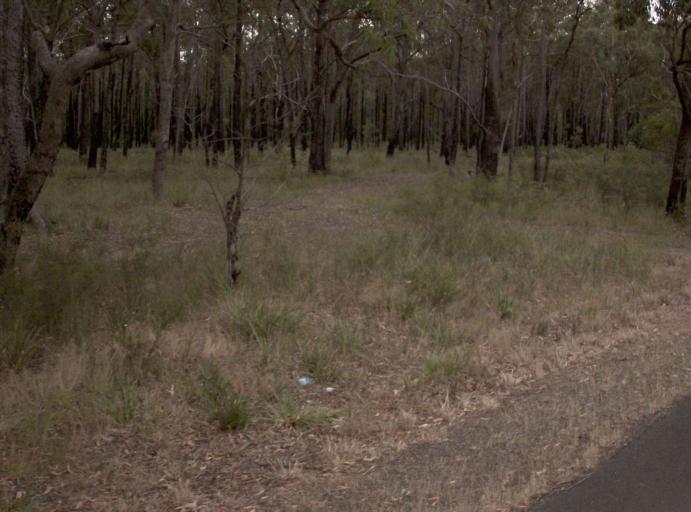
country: AU
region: Victoria
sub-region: Wellington
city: Sale
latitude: -38.4036
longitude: 146.9678
